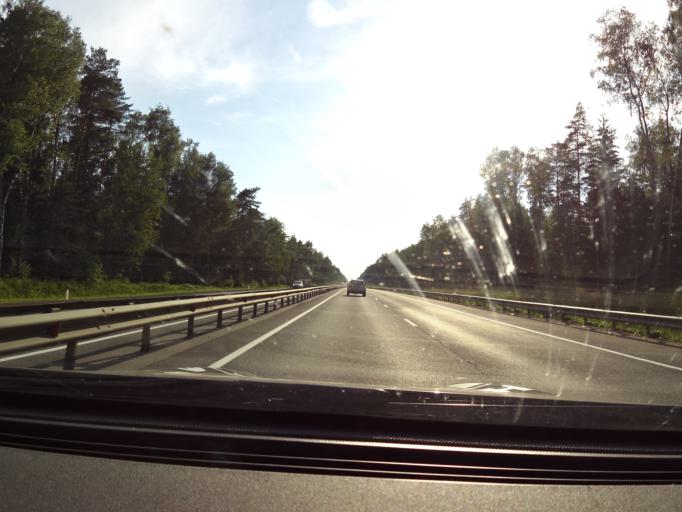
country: RU
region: Vladimir
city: Stepantsevo
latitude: 56.2231
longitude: 41.5661
